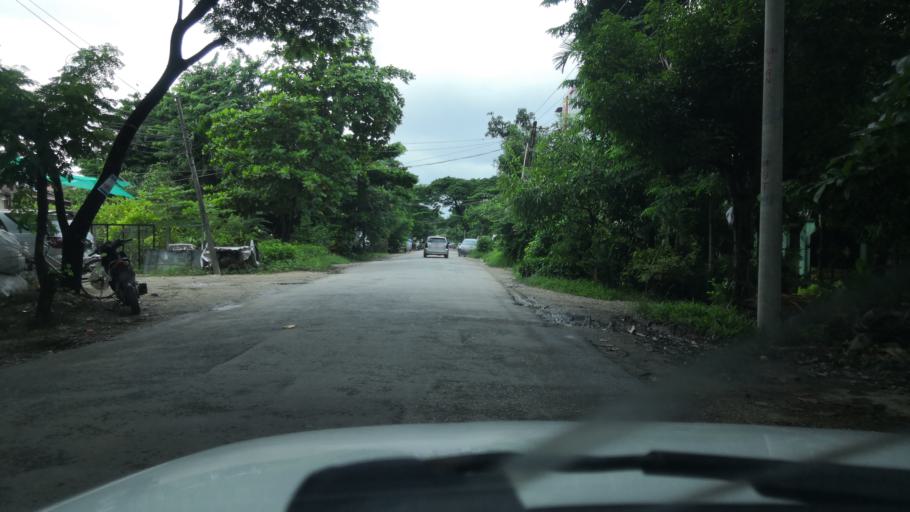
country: MM
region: Yangon
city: Yangon
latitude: 16.8795
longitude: 96.1803
